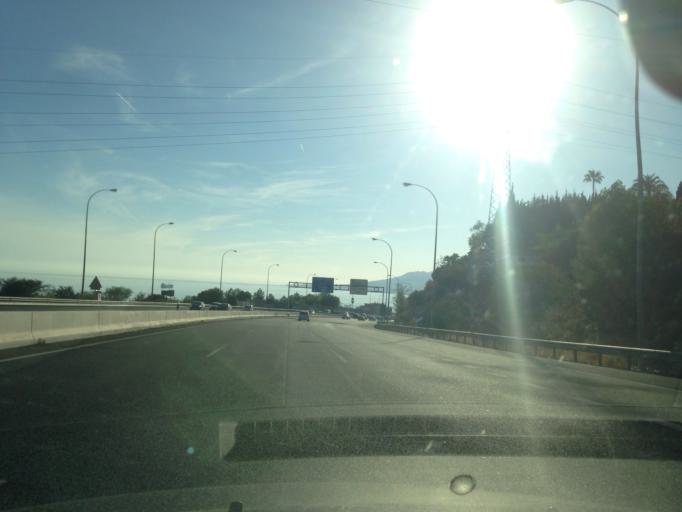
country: ES
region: Andalusia
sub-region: Provincia de Malaga
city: Malaga
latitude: 36.7305
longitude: -4.3587
